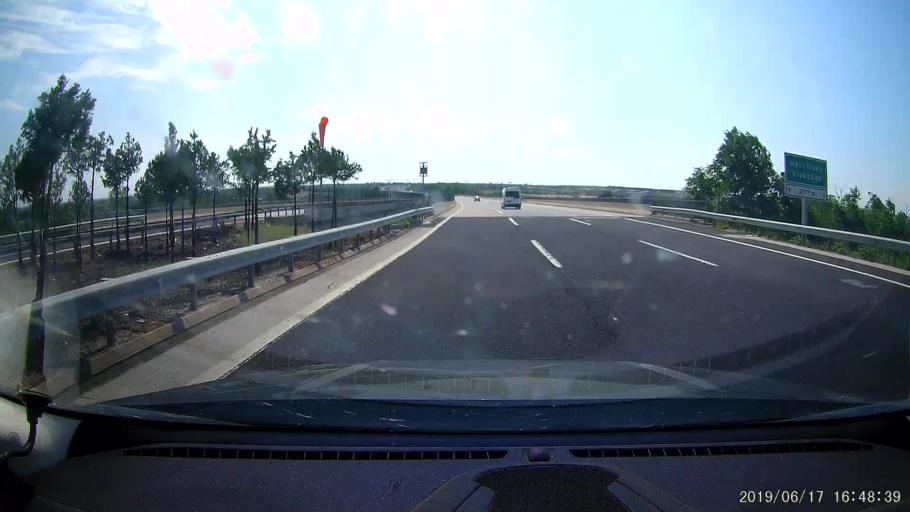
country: TR
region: Kirklareli
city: Babaeski
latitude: 41.5068
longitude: 27.1351
